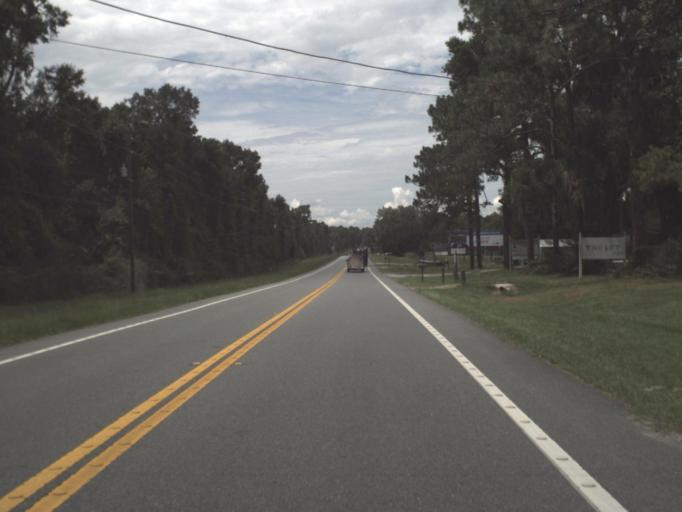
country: US
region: Florida
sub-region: Citrus County
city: Hernando
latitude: 28.9505
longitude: -82.3775
